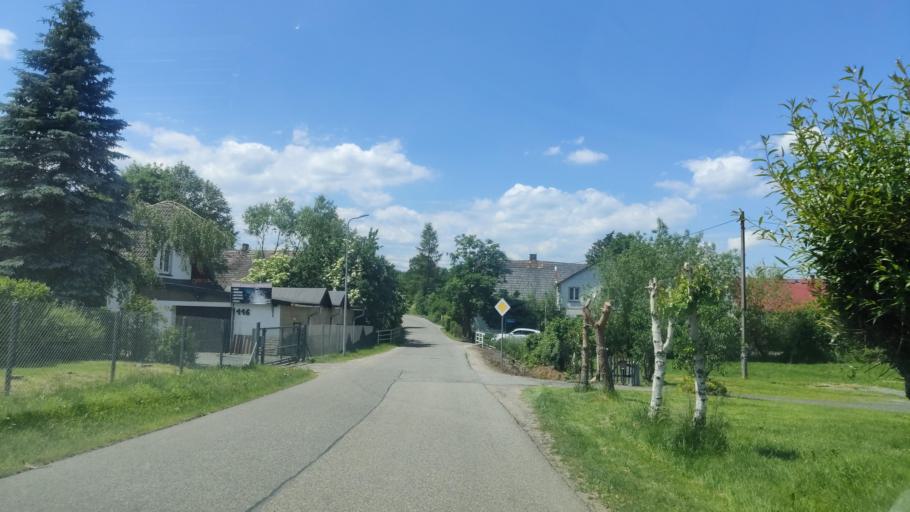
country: PL
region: Lower Silesian Voivodeship
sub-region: Powiat jeleniogorski
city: Myslakowice
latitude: 50.8173
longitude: 15.7984
